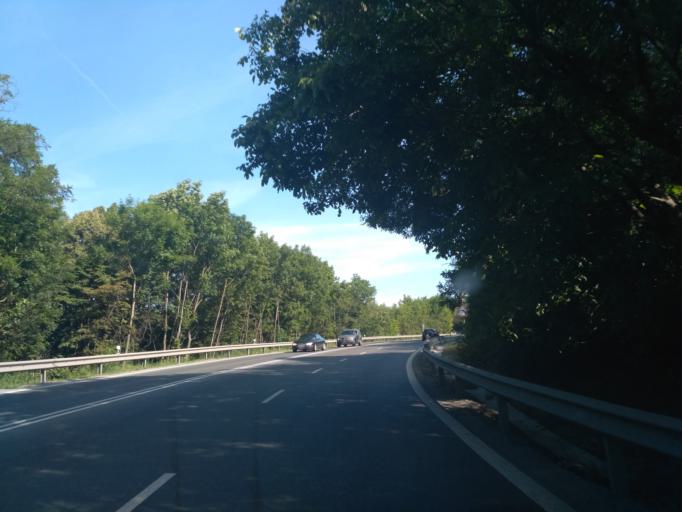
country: SK
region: Kosicky
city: Kosice
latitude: 48.7231
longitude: 21.2889
